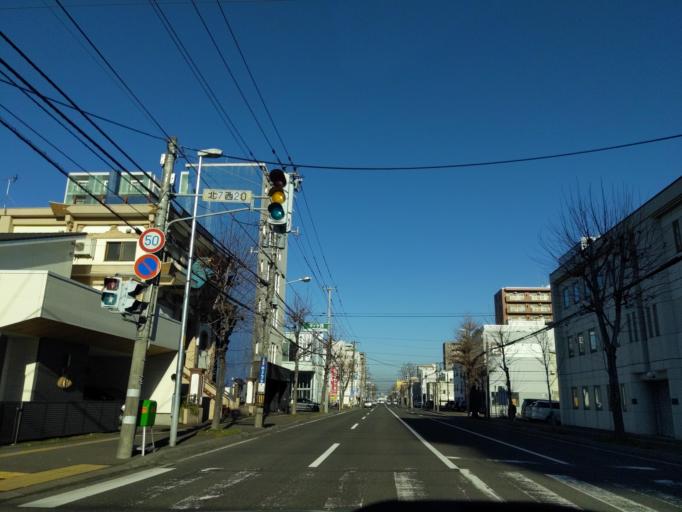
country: JP
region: Hokkaido
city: Sapporo
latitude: 43.0657
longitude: 141.3249
